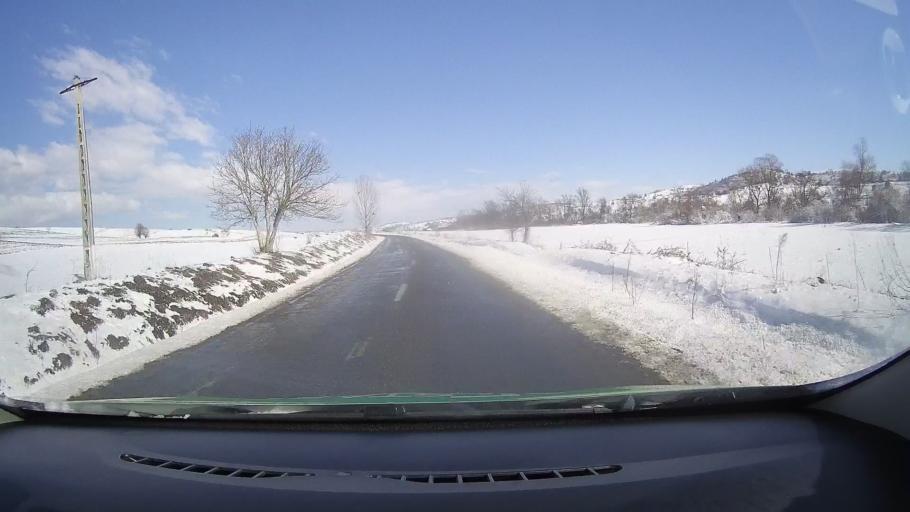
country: RO
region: Sibiu
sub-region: Comuna Vurpar
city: Vurpar
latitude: 45.8800
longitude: 24.3246
